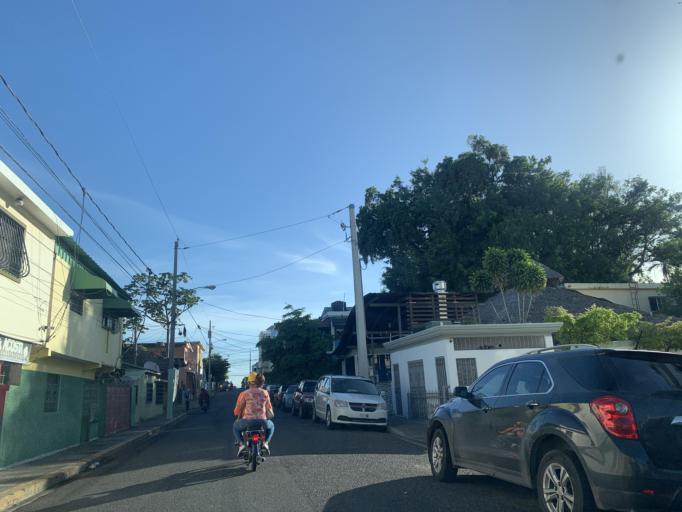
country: DO
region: Puerto Plata
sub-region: Puerto Plata
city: Puerto Plata
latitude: 19.7948
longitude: -70.6902
